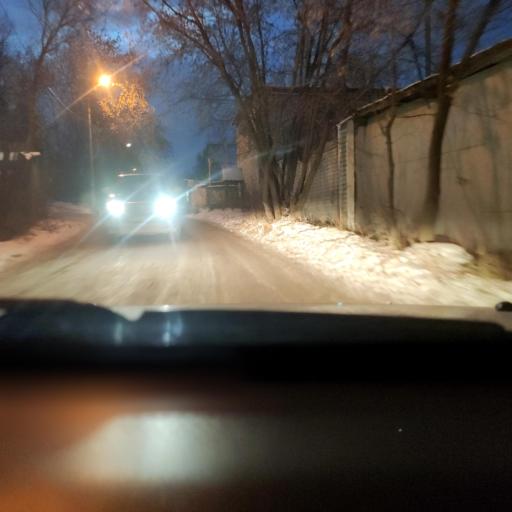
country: RU
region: Perm
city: Perm
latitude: 58.0380
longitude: 56.3233
